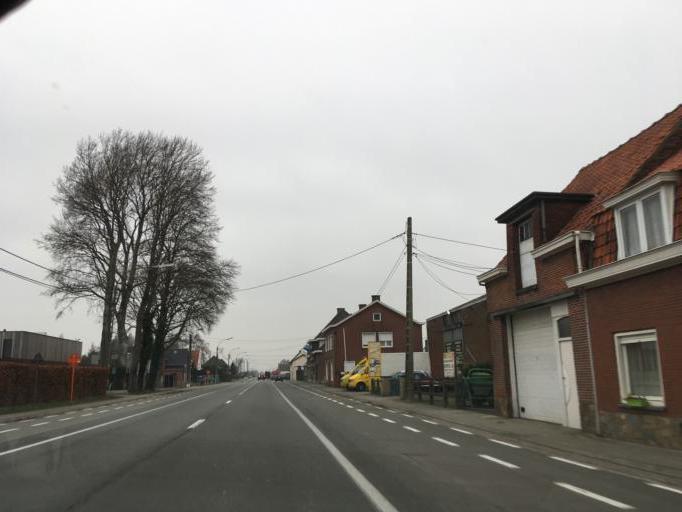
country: BE
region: Flanders
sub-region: Provincie West-Vlaanderen
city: Pittem
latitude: 50.9634
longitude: 3.2442
